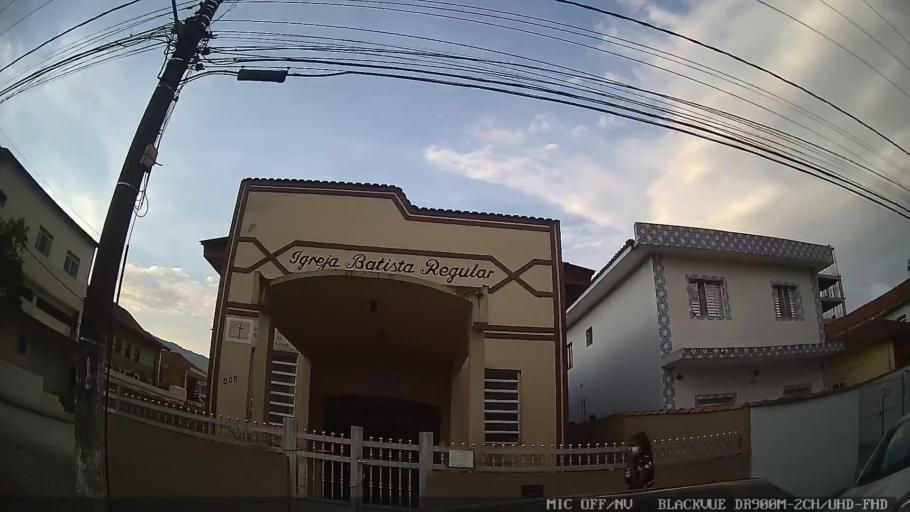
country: BR
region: Sao Paulo
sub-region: Cubatao
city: Cubatao
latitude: -23.8955
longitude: -46.4263
